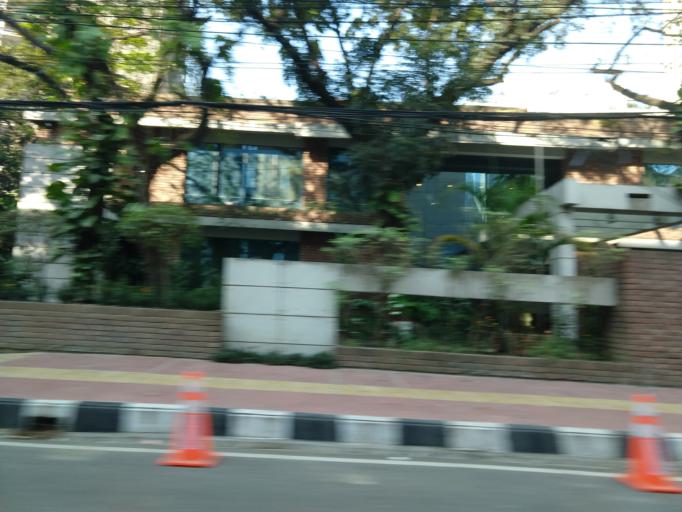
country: BD
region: Dhaka
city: Paltan
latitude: 23.7948
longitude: 90.4122
